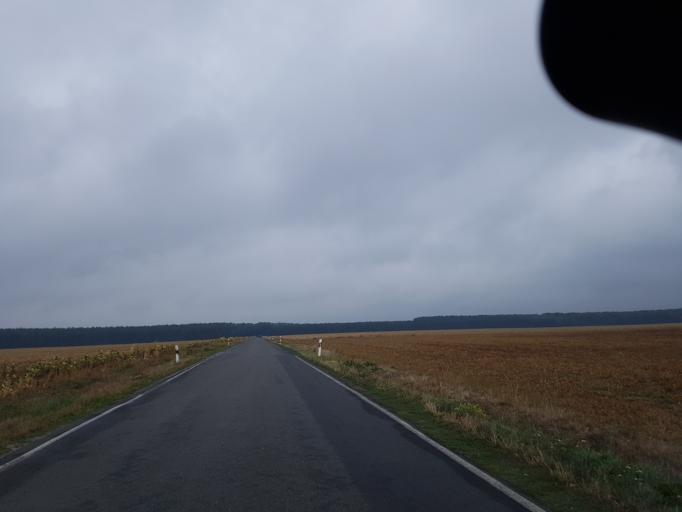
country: DE
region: Brandenburg
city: Gorzke
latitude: 52.1445
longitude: 12.3217
